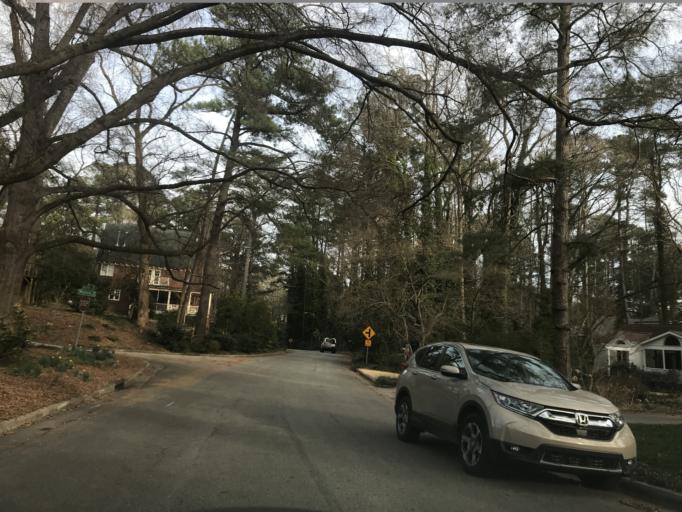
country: US
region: North Carolina
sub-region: Wake County
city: West Raleigh
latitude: 35.7973
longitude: -78.6703
